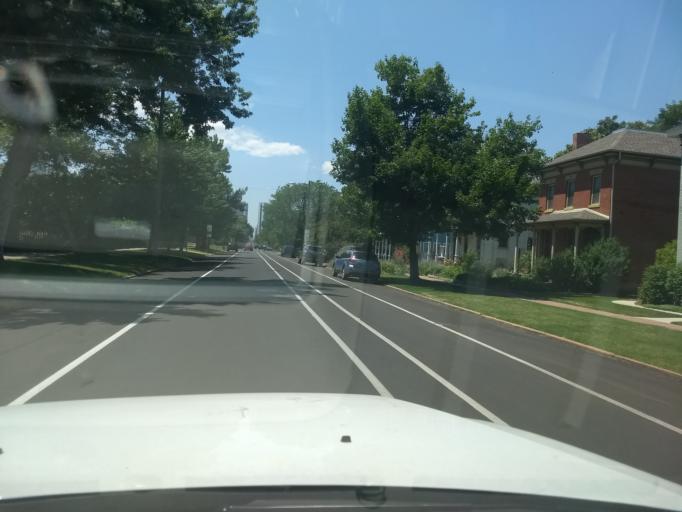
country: US
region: Colorado
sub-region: Denver County
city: Denver
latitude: 39.7567
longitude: -104.9808
